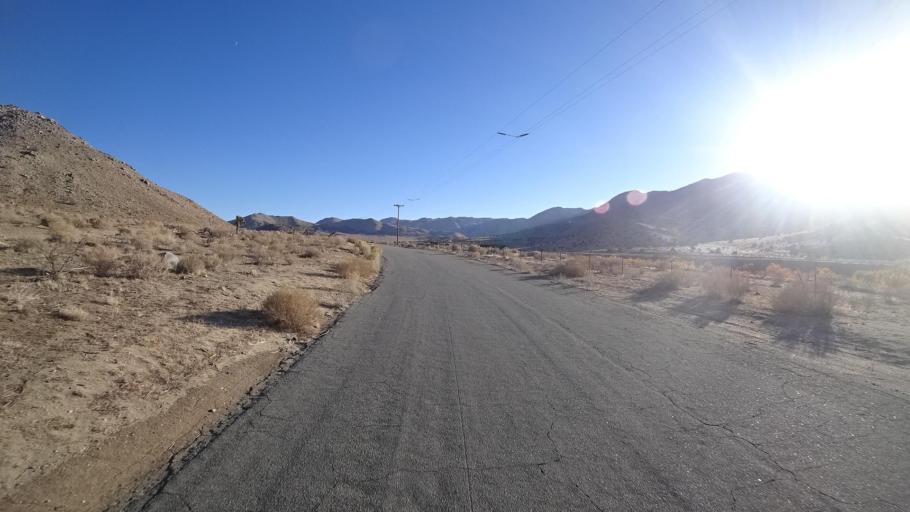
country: US
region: California
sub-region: Kern County
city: Weldon
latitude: 35.5706
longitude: -118.2502
